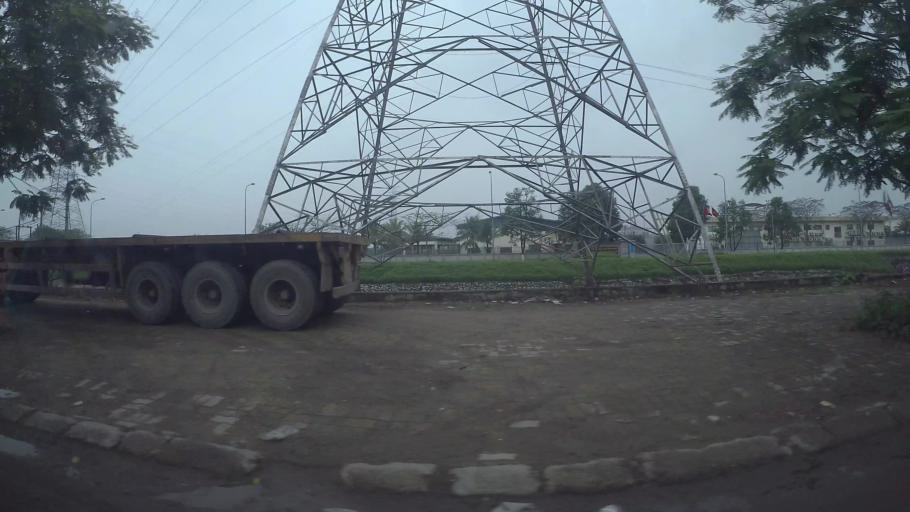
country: VN
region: Ha Noi
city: Van Dien
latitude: 20.9768
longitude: 105.8654
